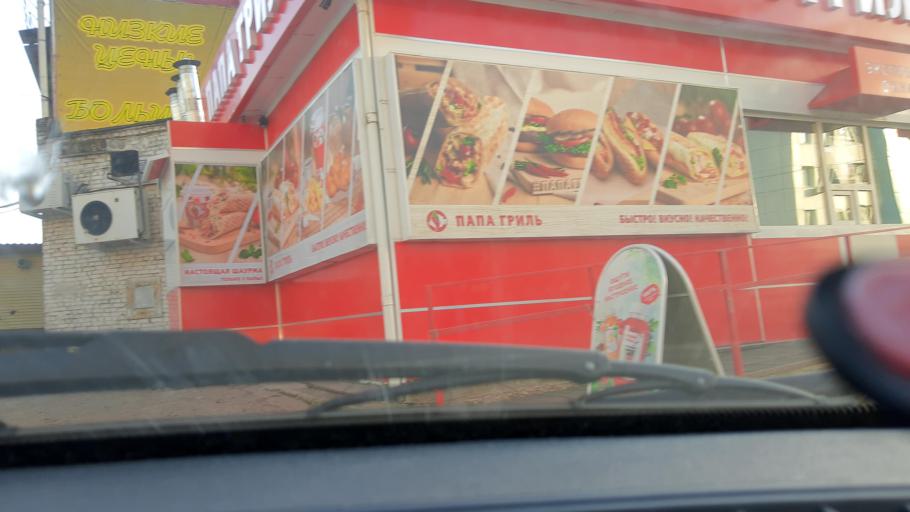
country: RU
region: Bashkortostan
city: Ufa
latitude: 54.7355
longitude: 55.9920
